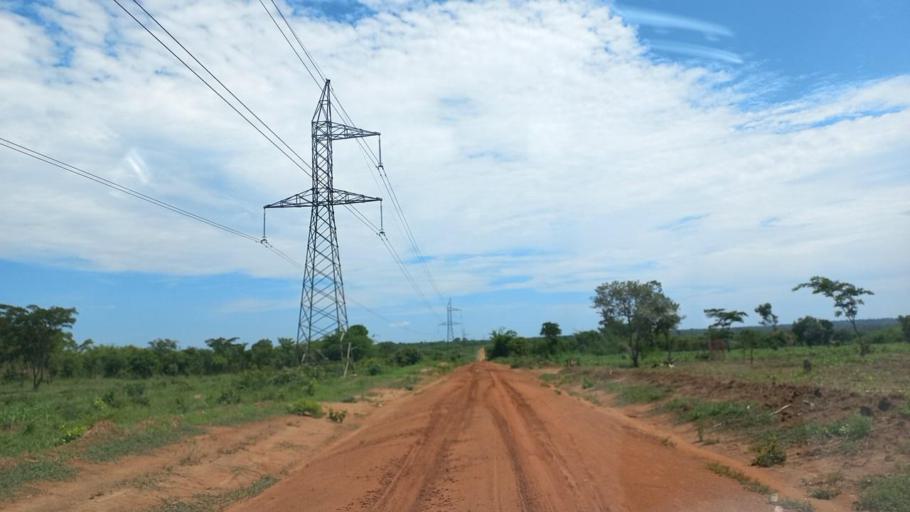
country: ZM
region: Copperbelt
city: Kitwe
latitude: -12.8358
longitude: 28.3428
